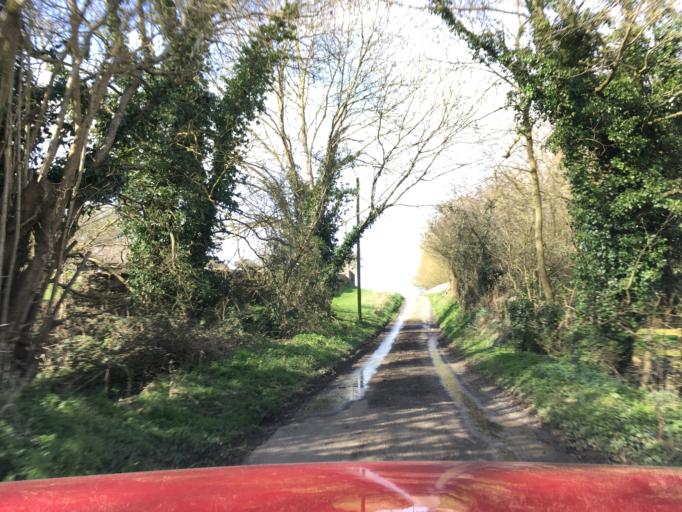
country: GB
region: England
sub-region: Wiltshire
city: Chippenham
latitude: 51.4985
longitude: -2.1517
